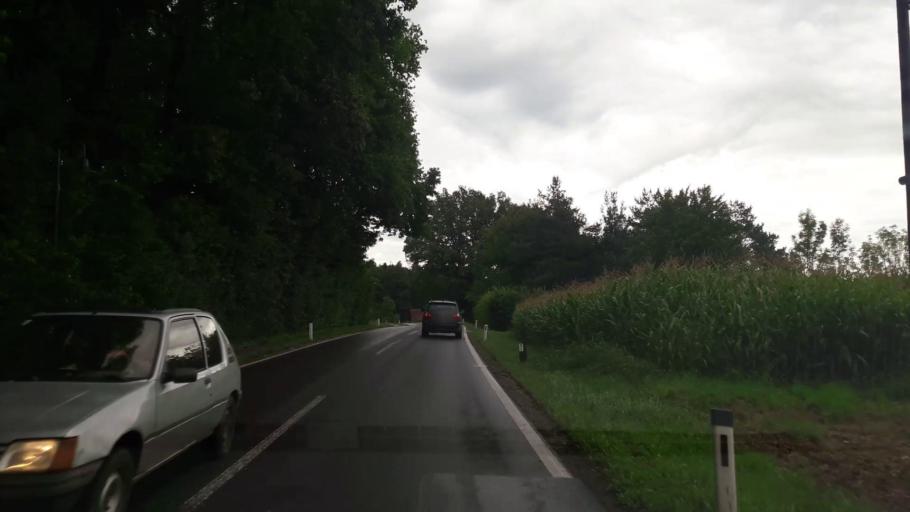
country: AT
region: Styria
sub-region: Politischer Bezirk Hartberg-Fuerstenfeld
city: Kaindorf
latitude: 47.2183
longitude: 15.9146
